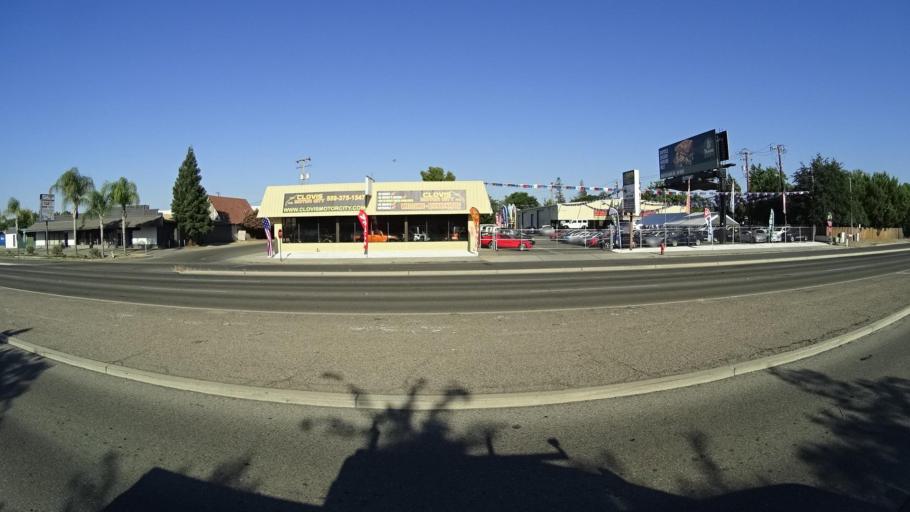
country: US
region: California
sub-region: Fresno County
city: Tarpey Village
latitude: 36.7863
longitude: -119.7002
